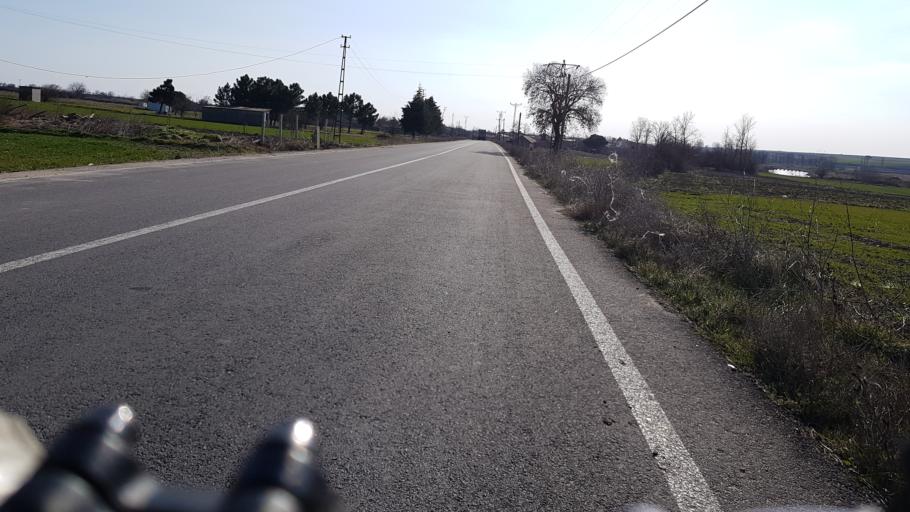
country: TR
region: Tekirdag
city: Velimese
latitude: 41.3493
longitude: 27.8385
